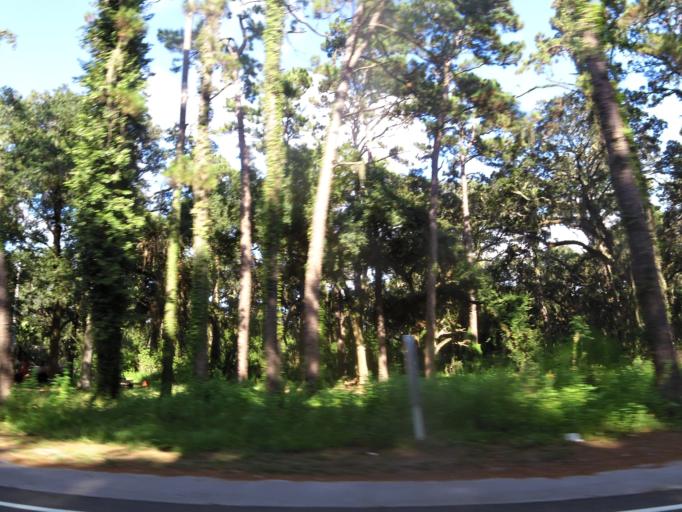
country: US
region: Georgia
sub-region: Glynn County
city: Saint Simon Mills
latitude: 31.2064
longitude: -81.3758
